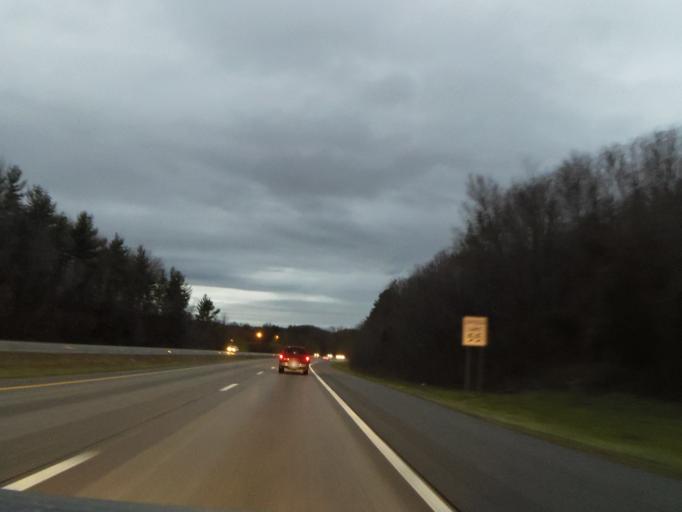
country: US
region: Tennessee
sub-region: Washington County
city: Oak Grove
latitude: 36.3629
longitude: -82.4083
